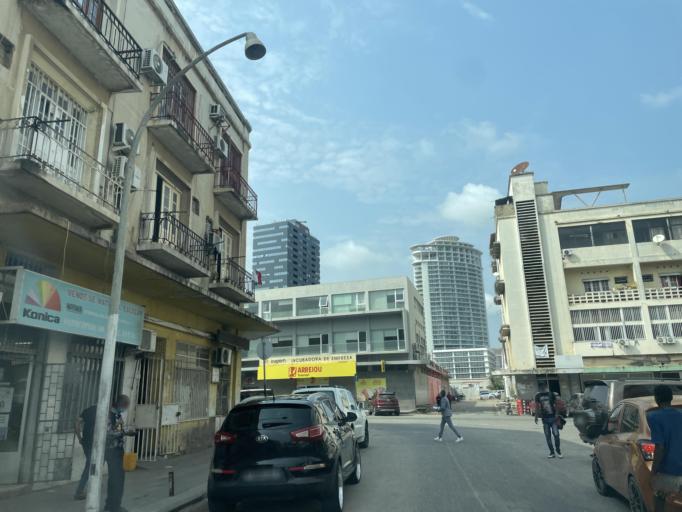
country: AO
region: Luanda
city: Luanda
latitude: -8.8060
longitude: 13.2414
